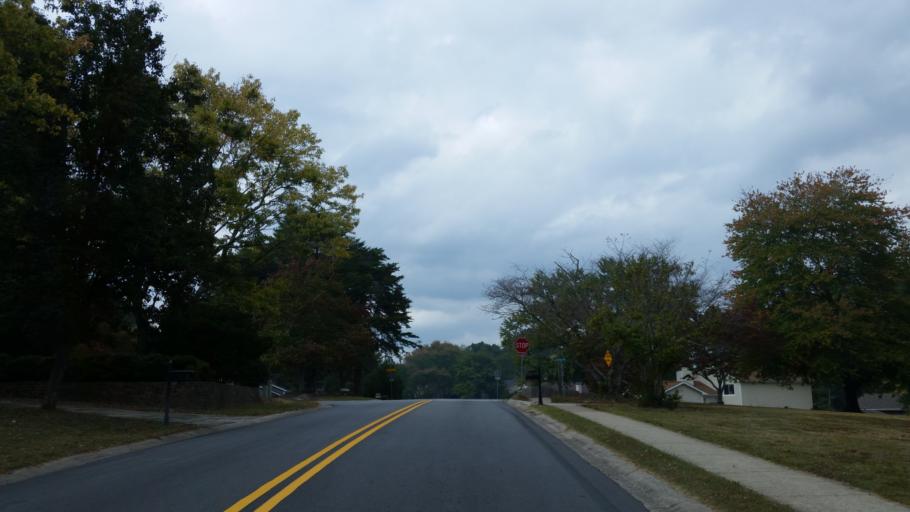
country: US
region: Georgia
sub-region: Fulton County
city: Sandy Springs
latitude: 33.9749
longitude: -84.4340
